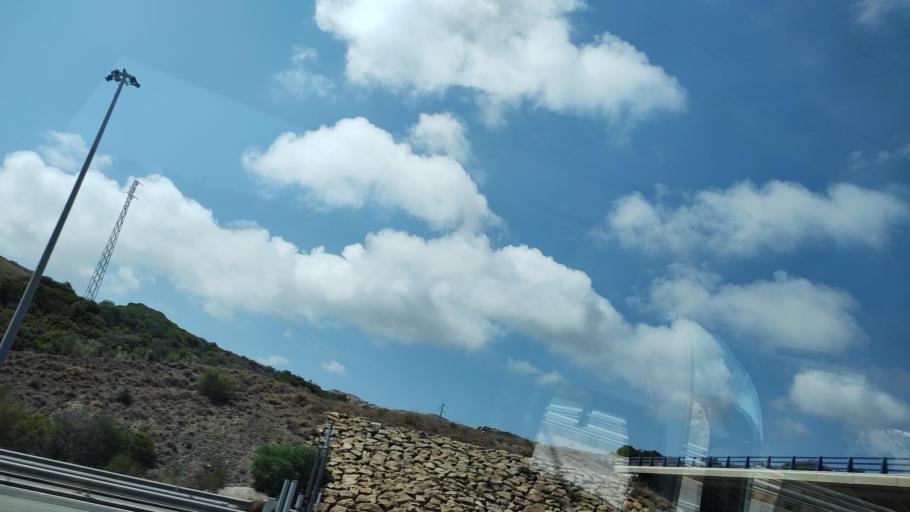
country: ES
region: Andalusia
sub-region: Provincia de Malaga
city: Manilva
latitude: 36.3772
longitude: -5.2640
